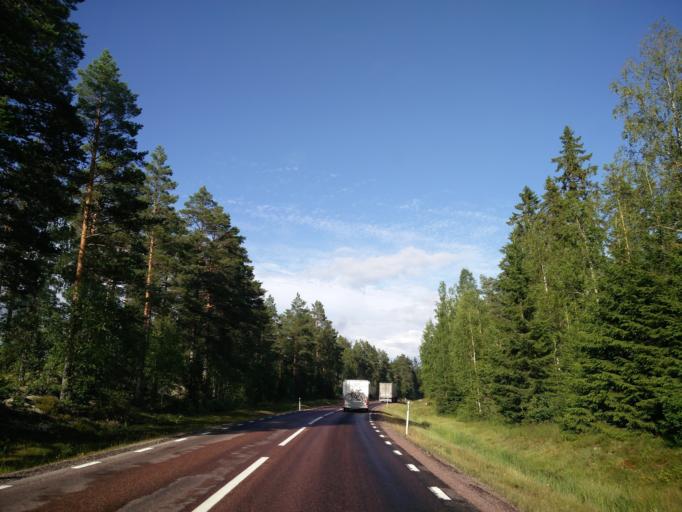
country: SE
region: Vaermland
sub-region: Hagfors Kommun
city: Ekshaerad
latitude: 60.4811
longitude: 13.3868
